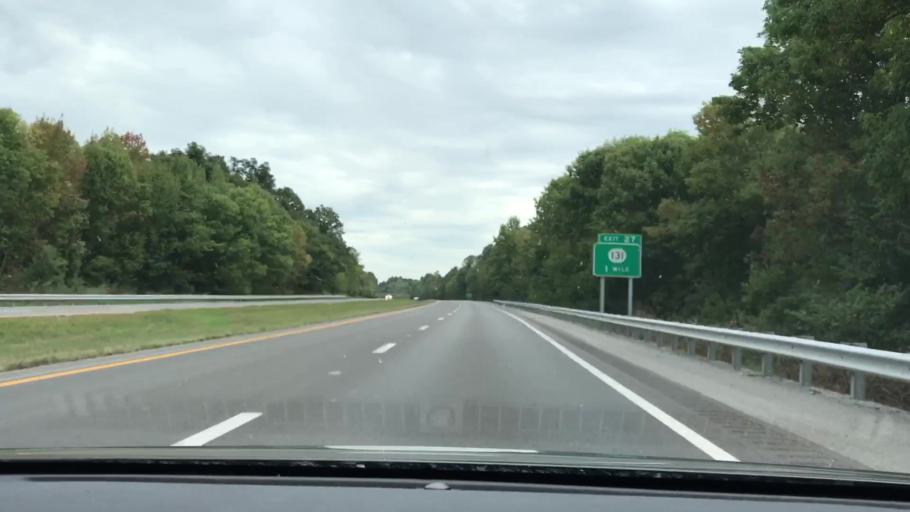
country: US
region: Kentucky
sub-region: Graves County
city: Mayfield
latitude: 36.7695
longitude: -88.6191
